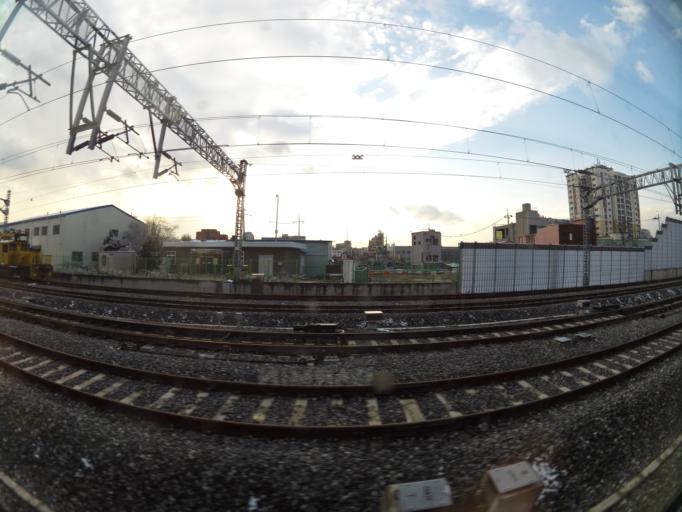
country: KR
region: Daejeon
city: Daejeon
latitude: 36.3361
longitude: 127.4322
